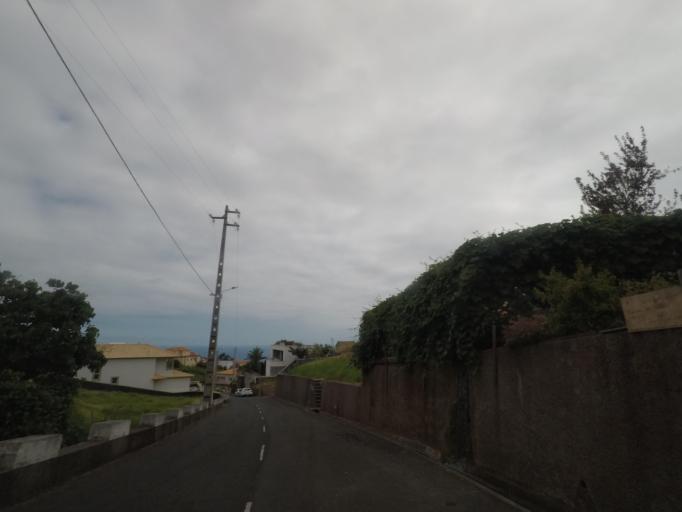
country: PT
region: Madeira
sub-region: Calheta
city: Estreito da Calheta
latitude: 32.7360
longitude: -17.1726
